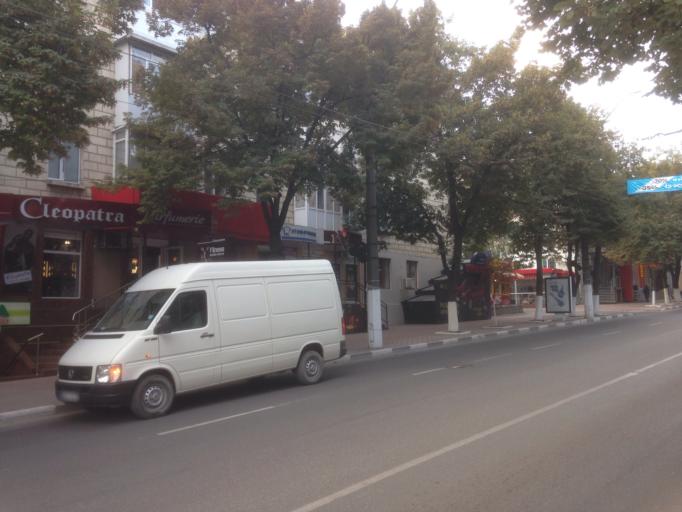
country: MD
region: Balti
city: Balti
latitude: 47.7637
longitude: 27.9304
